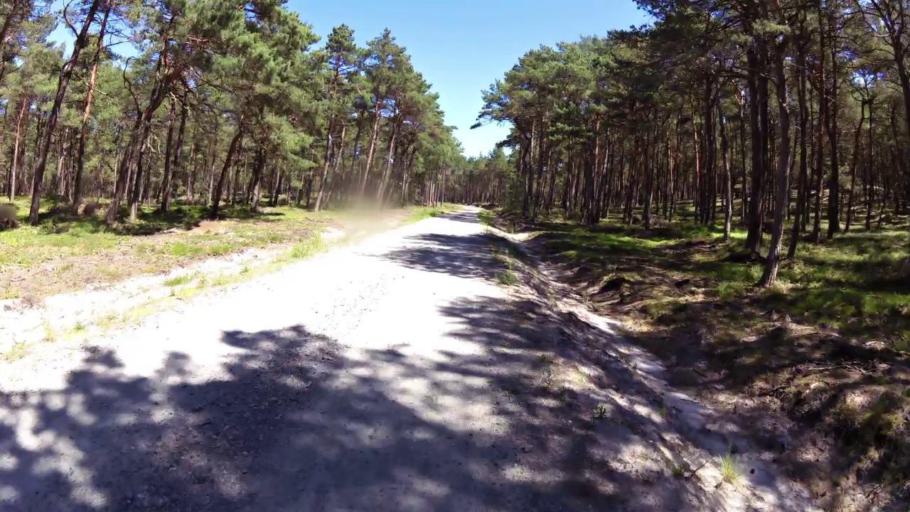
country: PL
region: West Pomeranian Voivodeship
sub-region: Powiat gryficki
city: Trzebiatow
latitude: 54.1138
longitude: 15.1978
